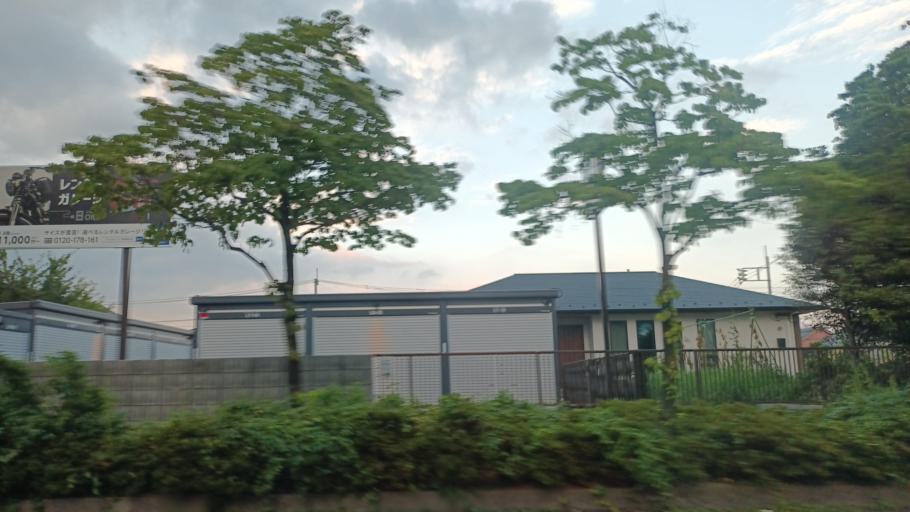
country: JP
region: Tokyo
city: Fussa
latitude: 35.7887
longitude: 139.3033
